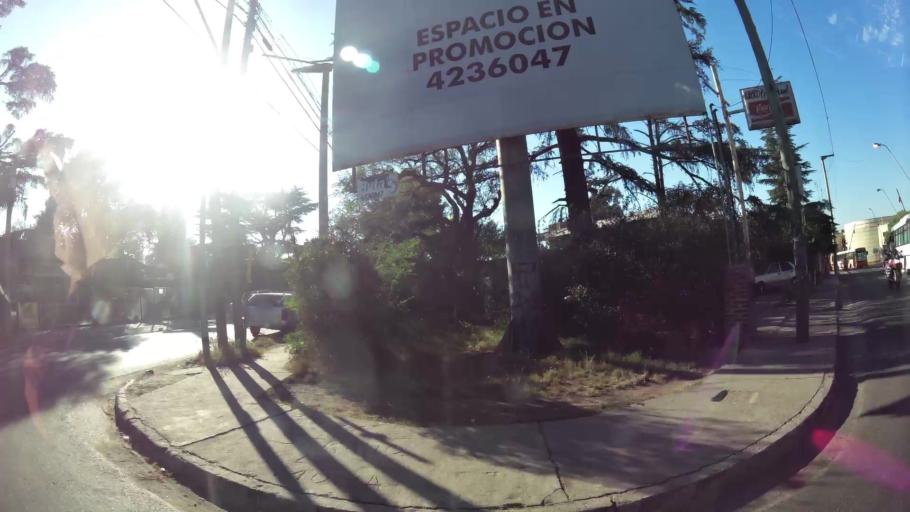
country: AR
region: Cordoba
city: Villa Allende
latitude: -31.3408
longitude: -64.2556
